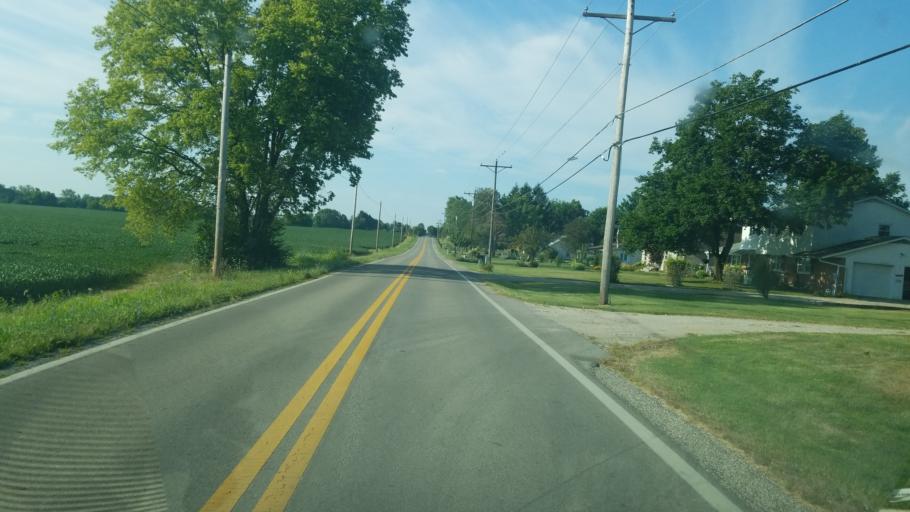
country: US
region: Ohio
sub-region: Franklin County
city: Lincoln Village
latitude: 39.9402
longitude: -83.1764
